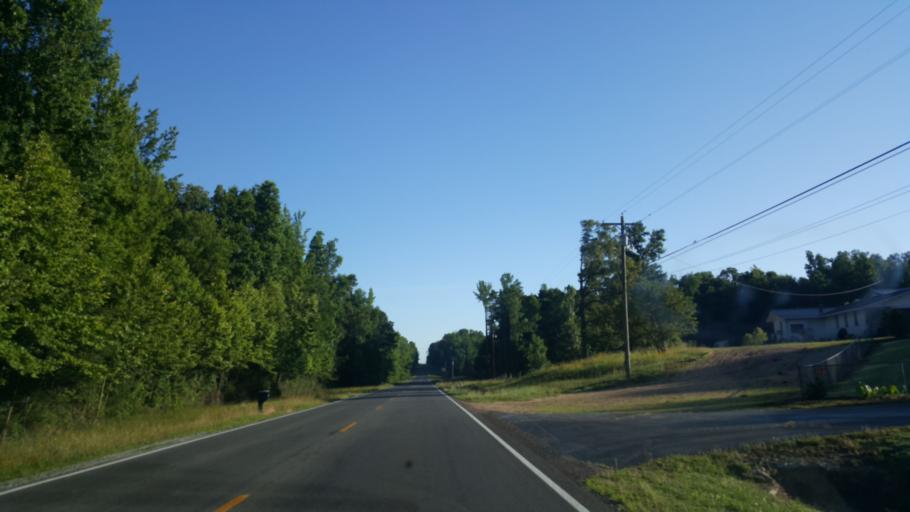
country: US
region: Tennessee
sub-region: Henderson County
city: Lexington
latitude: 35.5437
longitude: -88.3838
